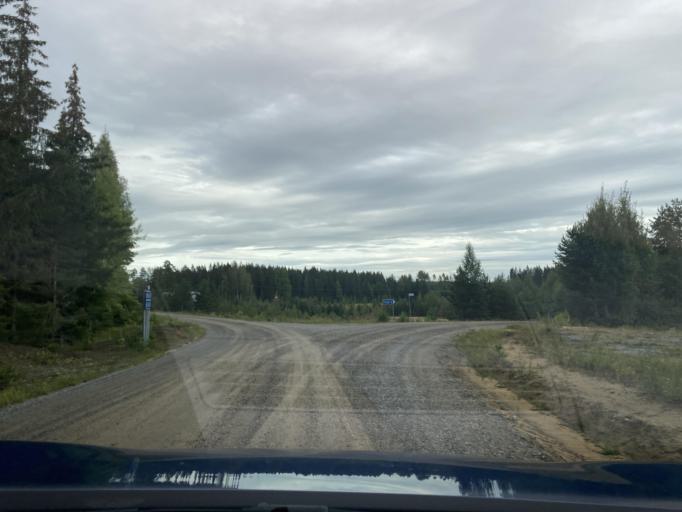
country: FI
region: Pirkanmaa
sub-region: Lounais-Pirkanmaa
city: Punkalaidun
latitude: 61.2464
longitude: 23.0451
